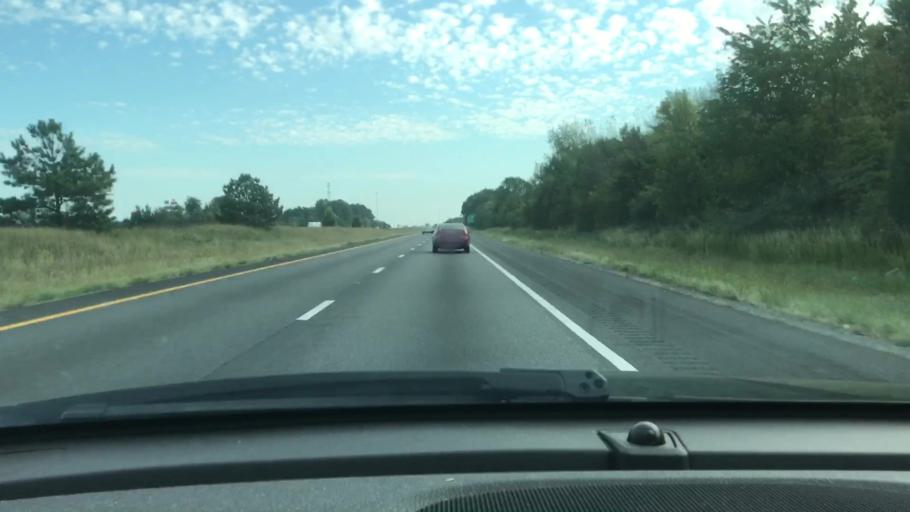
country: US
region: Tennessee
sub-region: Sumner County
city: White House
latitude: 36.4605
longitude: -86.6883
